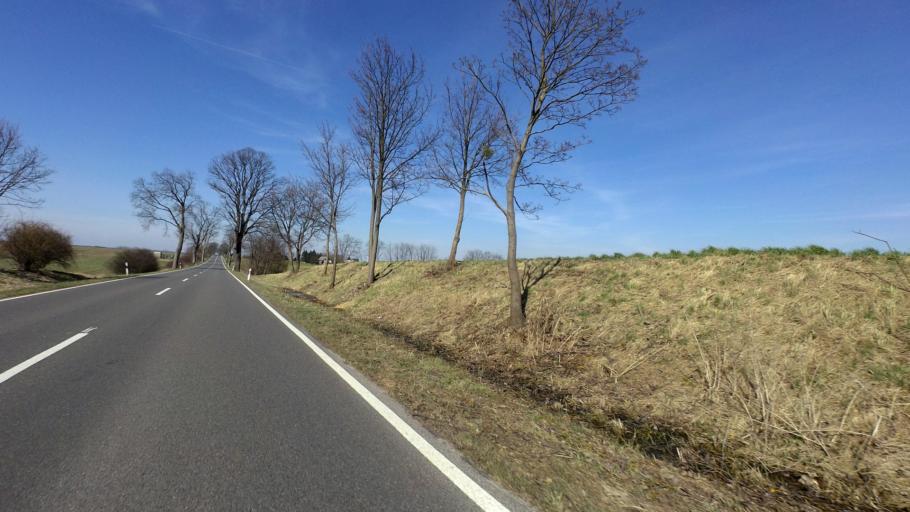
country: DE
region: Brandenburg
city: Protzel
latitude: 52.6114
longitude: 14.0210
